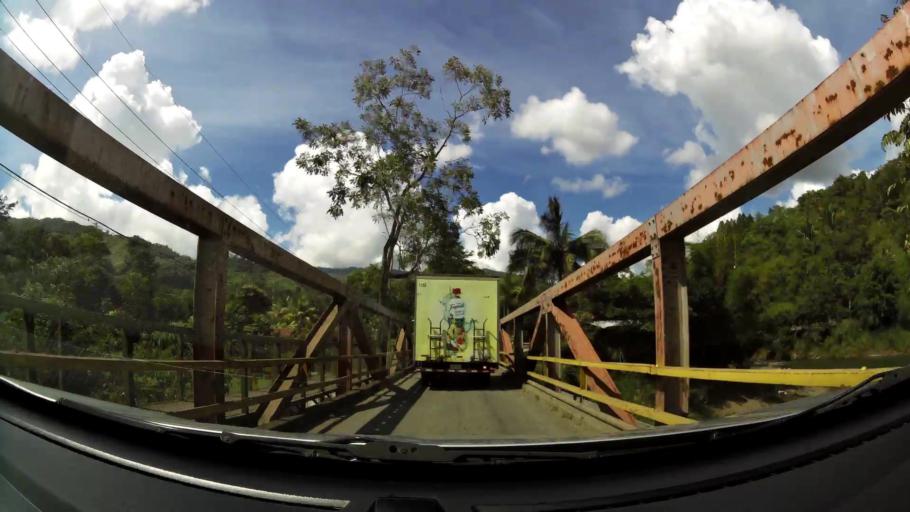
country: CR
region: San Jose
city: San Isidro
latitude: 9.3526
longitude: -83.7279
